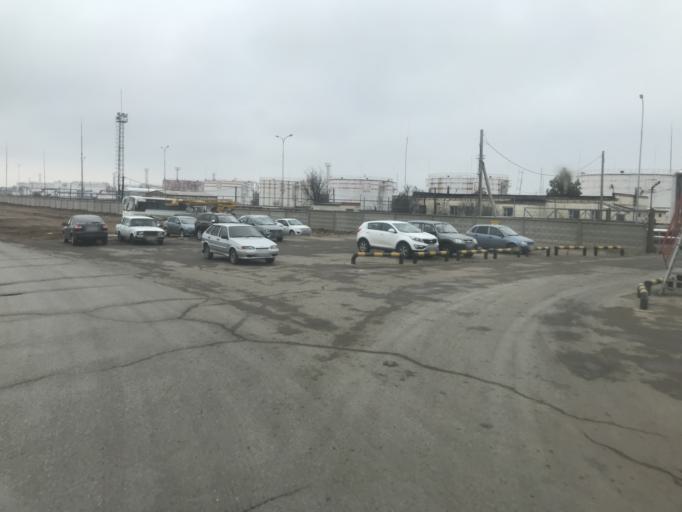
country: RU
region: Volgograd
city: Svetlyy Yar
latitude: 48.5037
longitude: 44.6467
